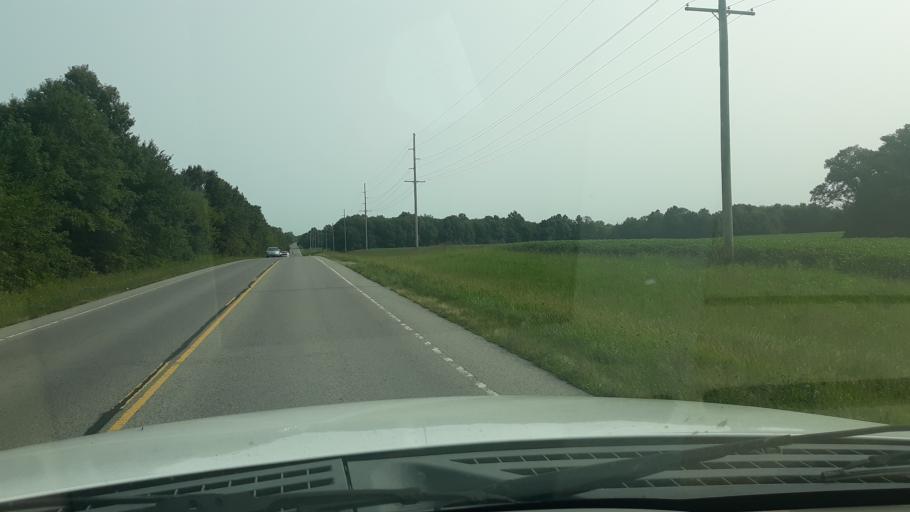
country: US
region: Illinois
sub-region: White County
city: Norris City
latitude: 38.0327
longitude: -88.2536
